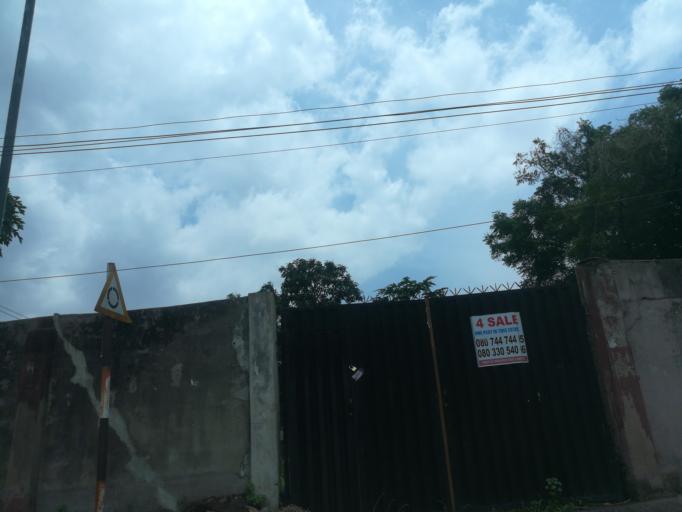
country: NG
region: Lagos
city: Somolu
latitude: 6.5513
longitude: 3.3619
